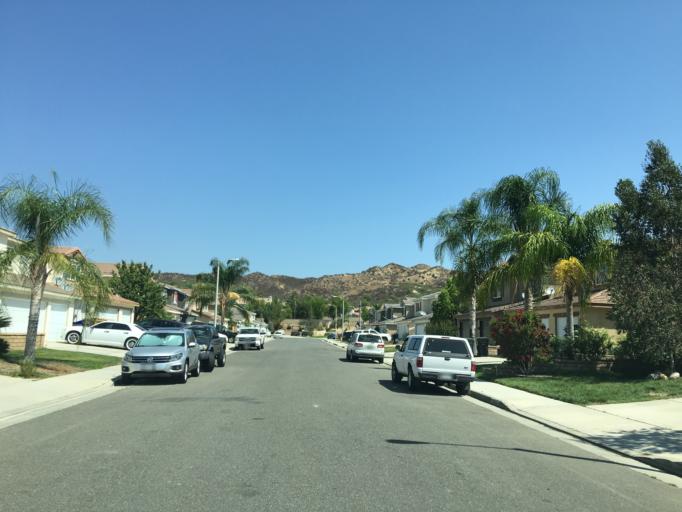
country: US
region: California
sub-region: Los Angeles County
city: Castaic
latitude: 34.4710
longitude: -118.6438
